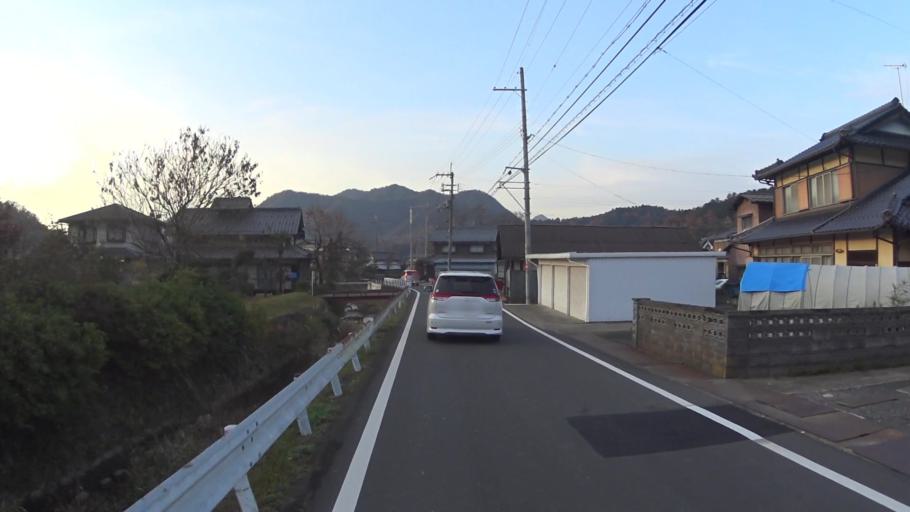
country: JP
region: Kyoto
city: Maizuru
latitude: 35.4796
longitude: 135.4417
